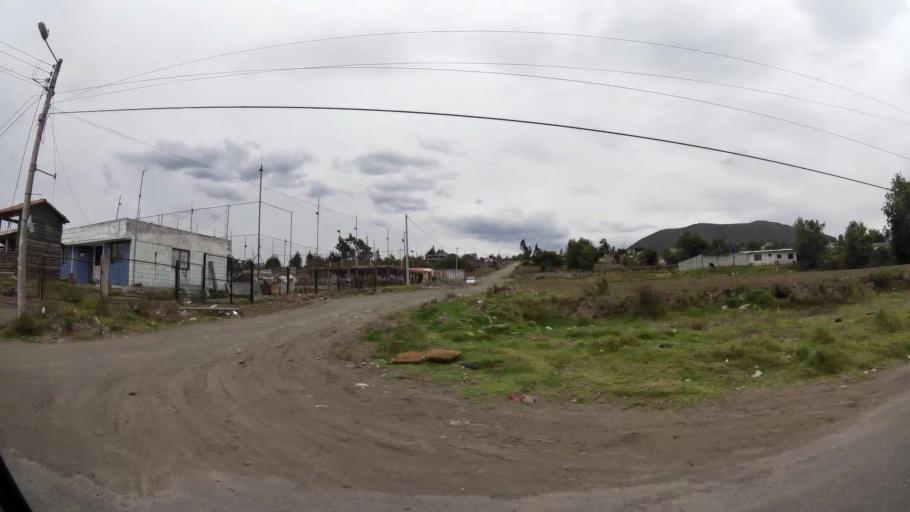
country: EC
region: Cotopaxi
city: Latacunga
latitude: -0.9533
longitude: -78.6017
